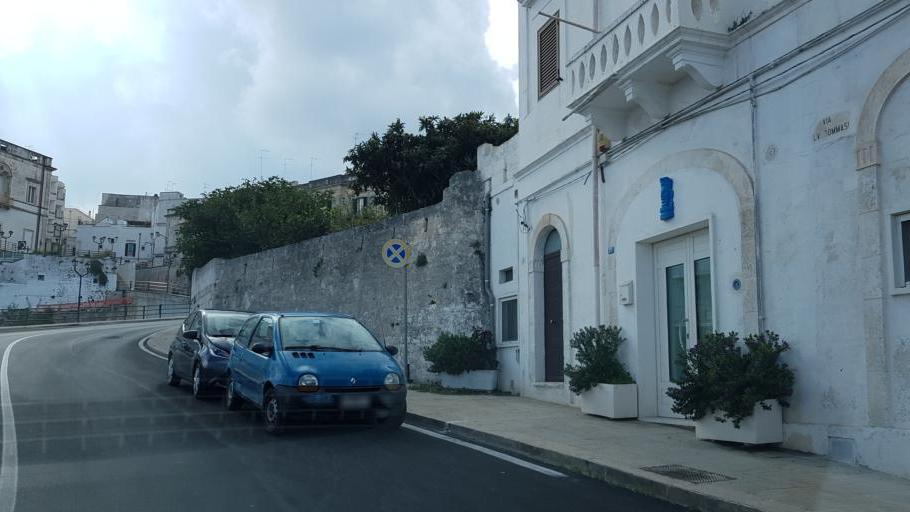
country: IT
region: Apulia
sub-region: Provincia di Brindisi
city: Ostuni
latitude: 40.7321
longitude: 17.5804
